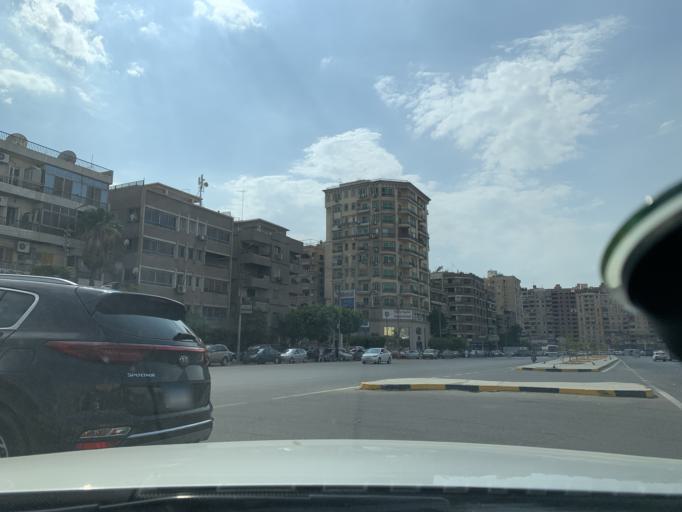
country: EG
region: Muhafazat al Qalyubiyah
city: Al Khankah
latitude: 30.1164
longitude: 31.3422
